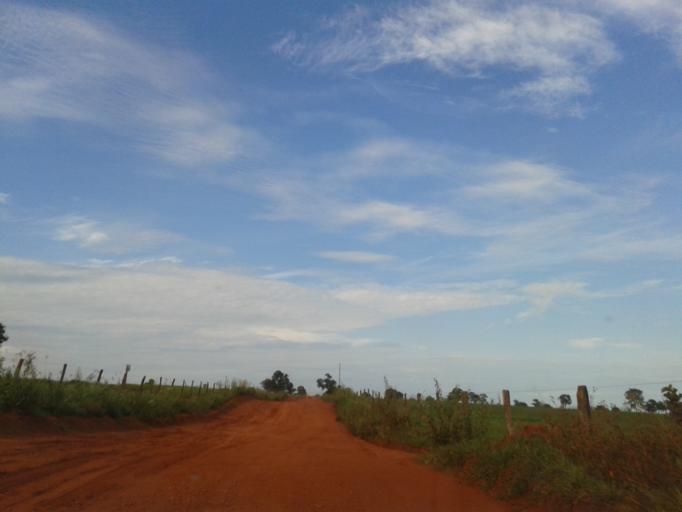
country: BR
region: Minas Gerais
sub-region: Santa Vitoria
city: Santa Vitoria
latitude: -19.1024
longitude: -50.5077
